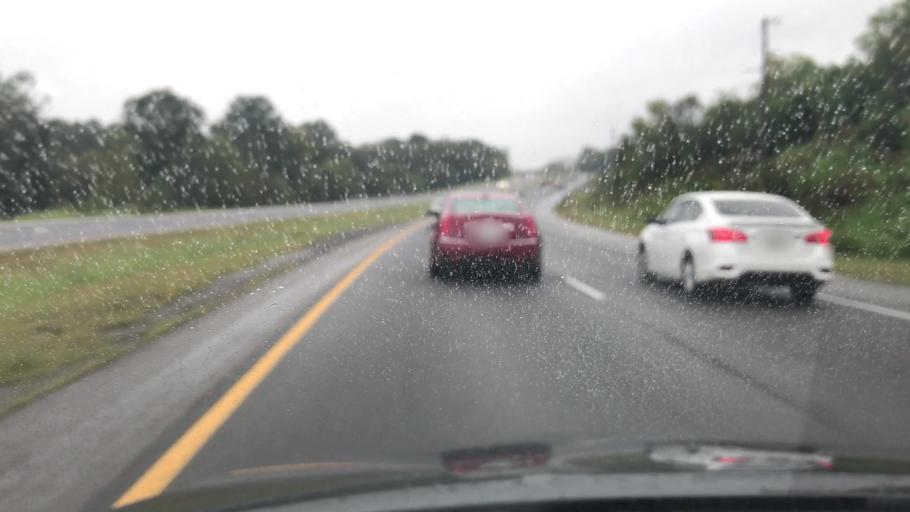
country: US
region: Tennessee
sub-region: Cheatham County
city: Ashland City
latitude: 36.2165
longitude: -86.9906
